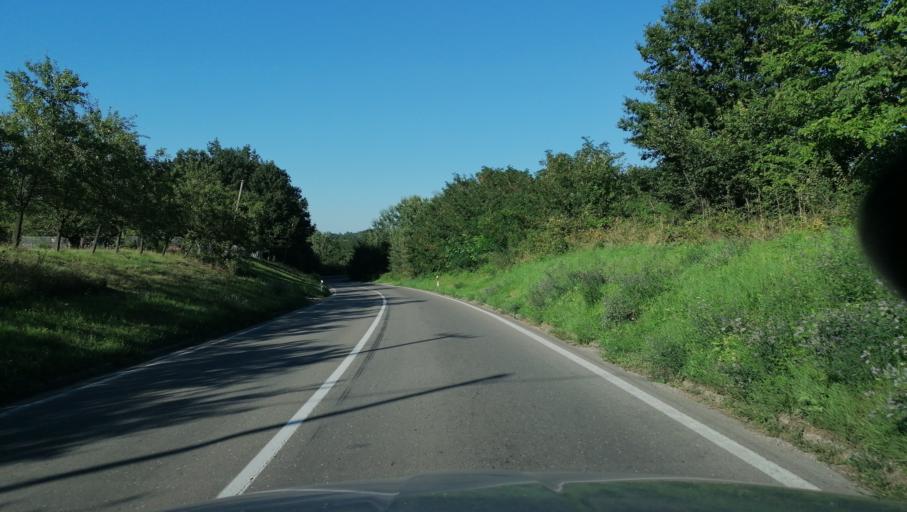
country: RS
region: Central Serbia
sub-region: Sumadijski Okrug
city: Knic
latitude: 43.8945
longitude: 20.6176
